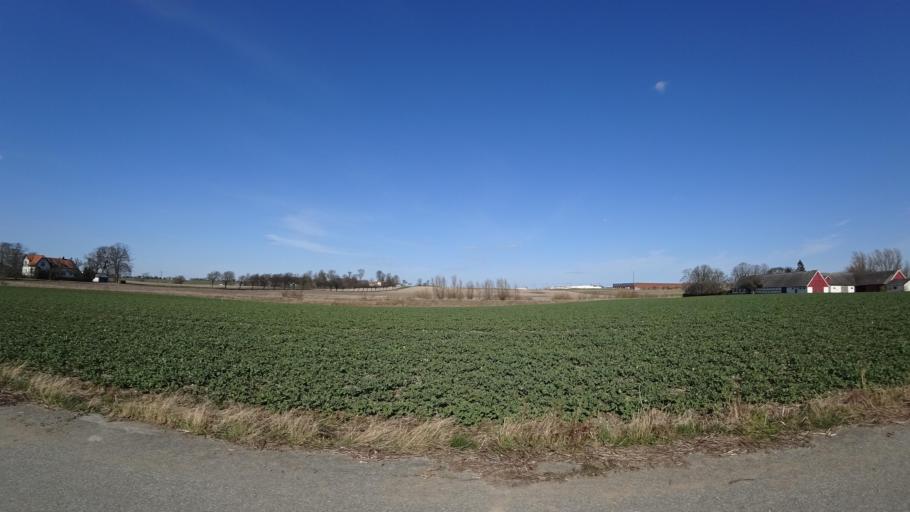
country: SE
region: Skane
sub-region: Staffanstorps Kommun
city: Staffanstorp
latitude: 55.6272
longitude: 13.1701
